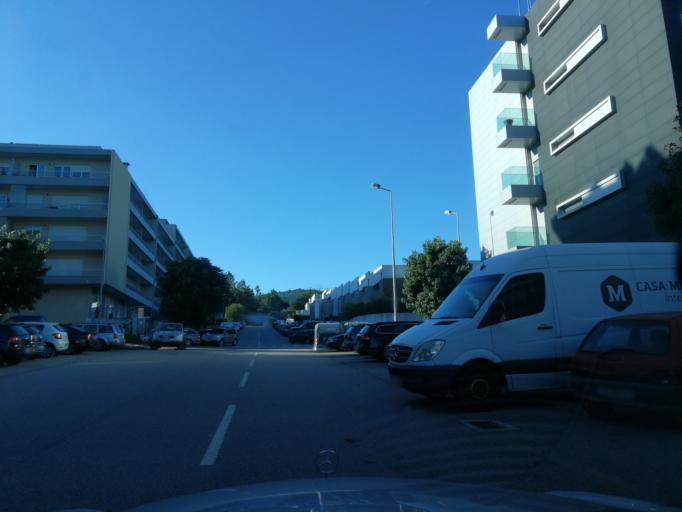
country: PT
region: Braga
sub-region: Braga
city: Braga
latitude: 41.5385
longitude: -8.3971
